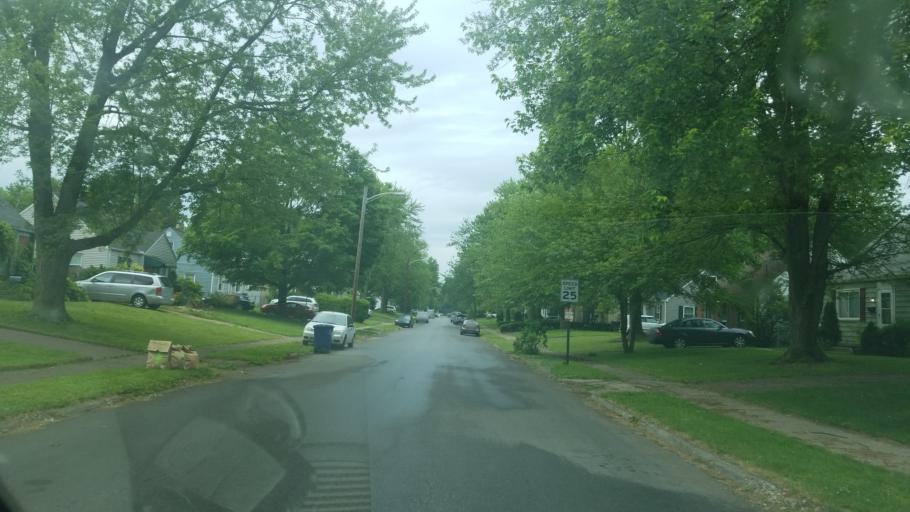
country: US
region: Ohio
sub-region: Franklin County
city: Minerva Park
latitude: 40.0293
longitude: -82.9778
